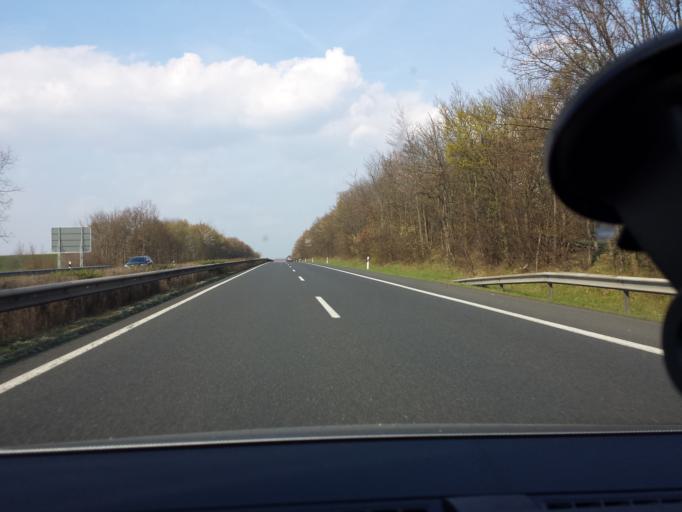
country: DE
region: Lower Saxony
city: Leiferde
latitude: 52.1937
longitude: 10.5220
